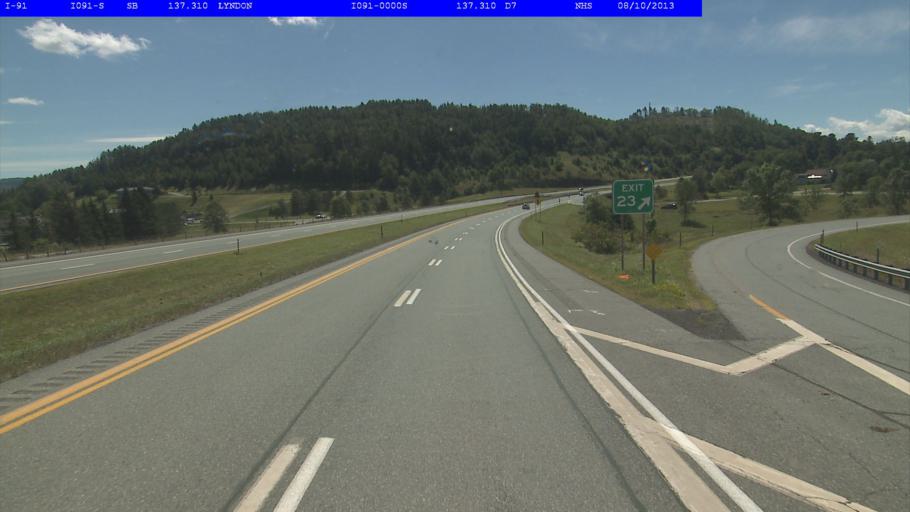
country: US
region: Vermont
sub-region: Caledonia County
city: Lyndon
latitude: 44.5193
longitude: -72.0074
